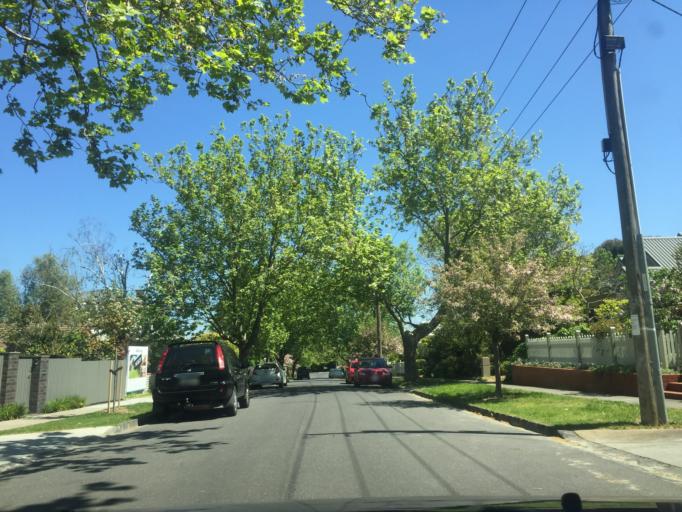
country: AU
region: Victoria
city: Mont Albert
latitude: -37.8189
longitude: 145.0933
